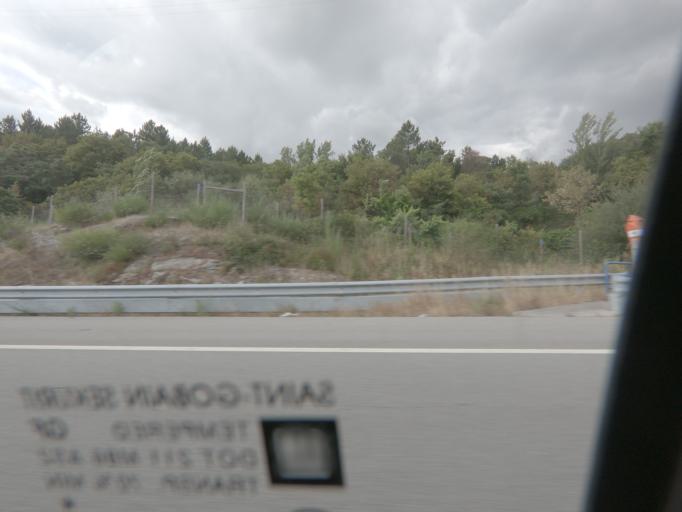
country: PT
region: Porto
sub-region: Amarante
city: Amarante
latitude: 41.2556
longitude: -8.0424
